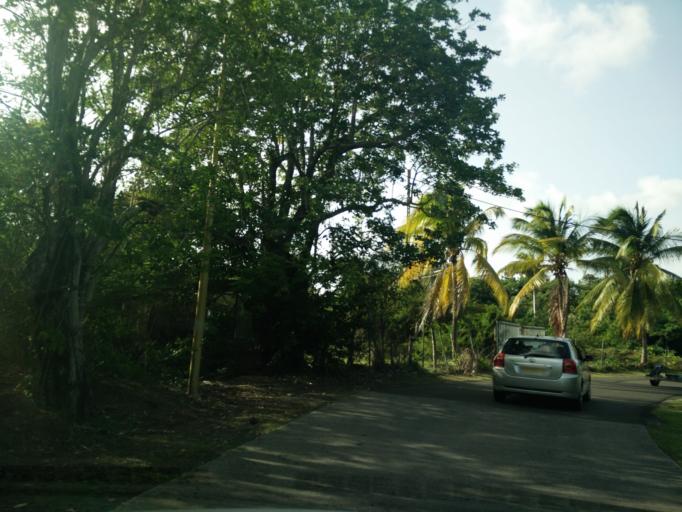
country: MQ
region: Martinique
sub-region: Martinique
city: Riviere-Pilote
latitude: 14.4692
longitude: -60.9081
